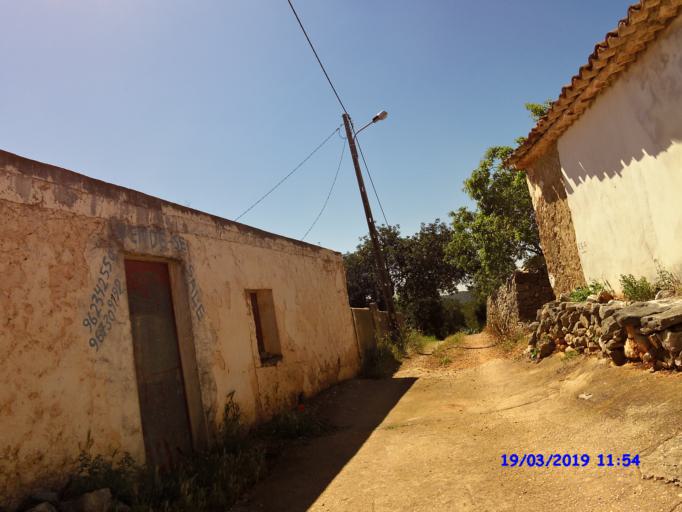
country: PT
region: Faro
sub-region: Loule
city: Boliqueime
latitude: 37.2095
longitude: -8.1464
